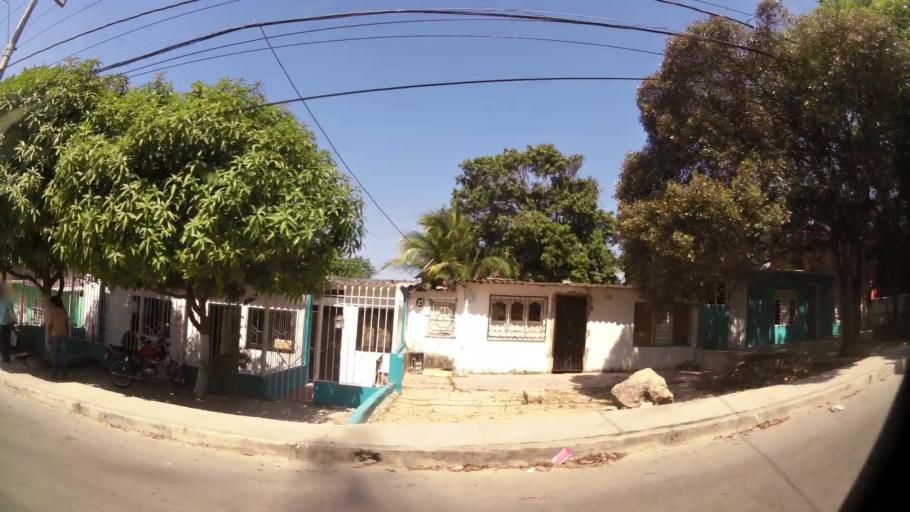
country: CO
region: Atlantico
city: Barranquilla
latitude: 10.9800
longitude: -74.8212
